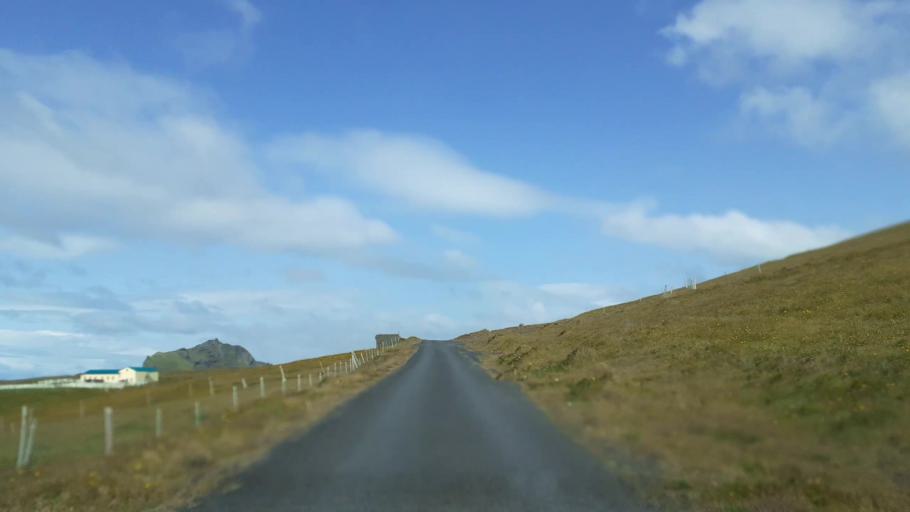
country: IS
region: South
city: Vestmannaeyjar
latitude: 63.4155
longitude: -20.2809
